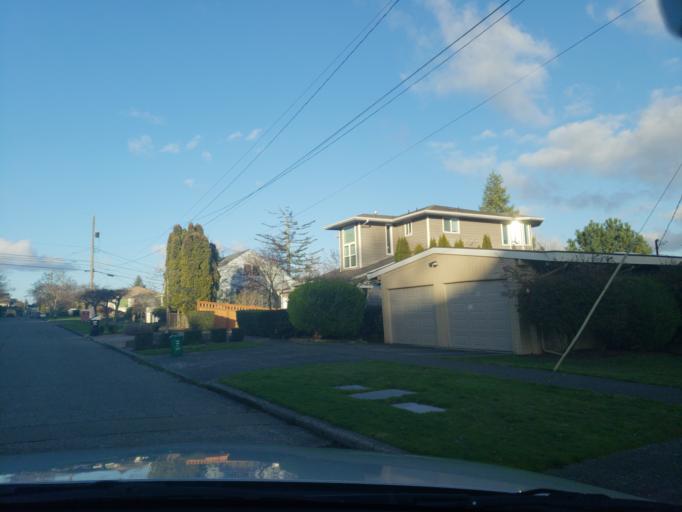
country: US
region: Washington
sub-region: King County
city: Seattle
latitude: 47.6378
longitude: -122.3904
